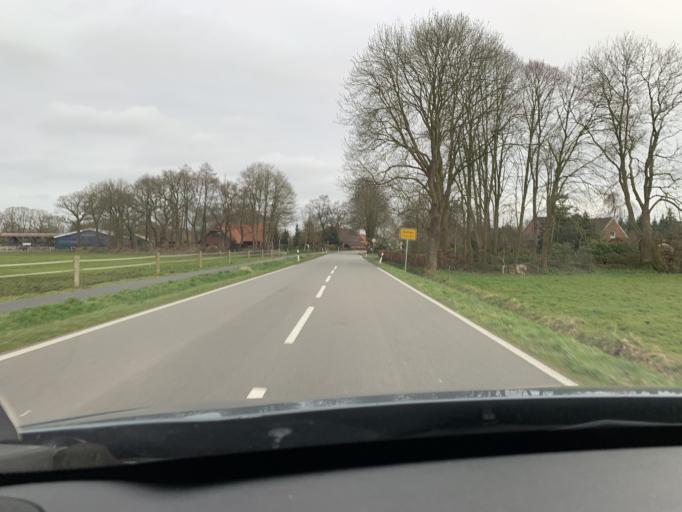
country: DE
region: Lower Saxony
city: Detern
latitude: 53.2576
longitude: 7.7110
